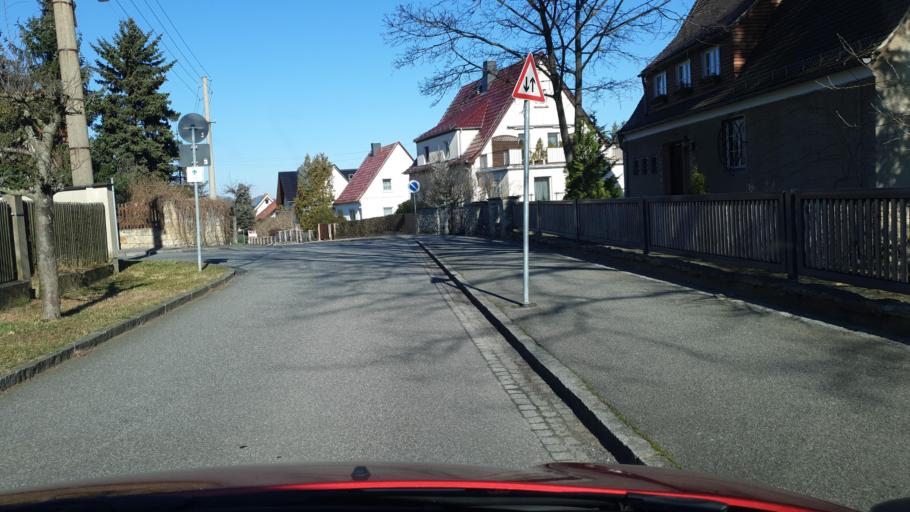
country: DE
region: Saxony
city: Moritzburg
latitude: 51.1609
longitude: 13.6825
